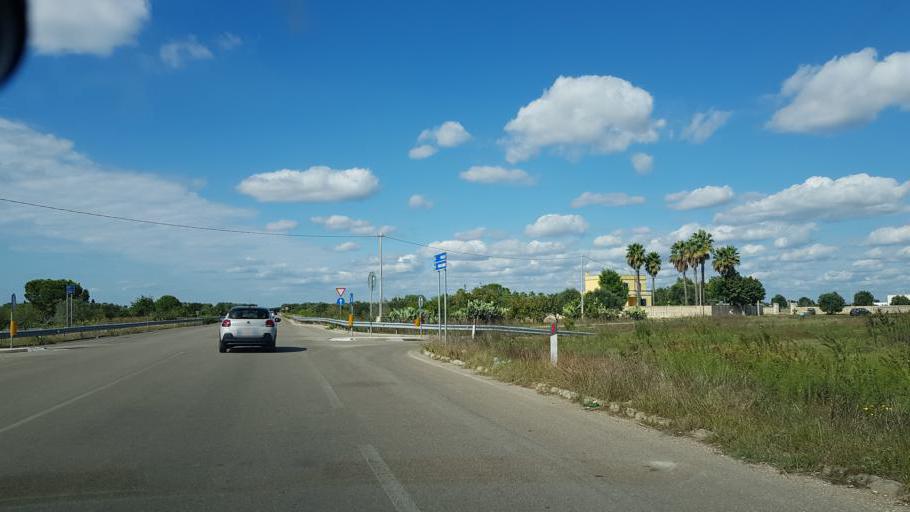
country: IT
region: Apulia
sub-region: Provincia di Lecce
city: Leverano
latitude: 40.3053
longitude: 18.0008
